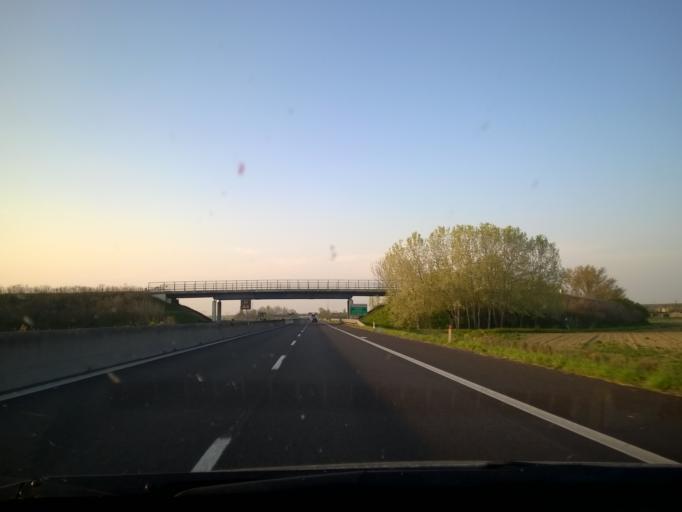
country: IT
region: Veneto
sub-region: Provincia di Rovigo
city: Occhiobello
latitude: 44.8942
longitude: 11.5702
